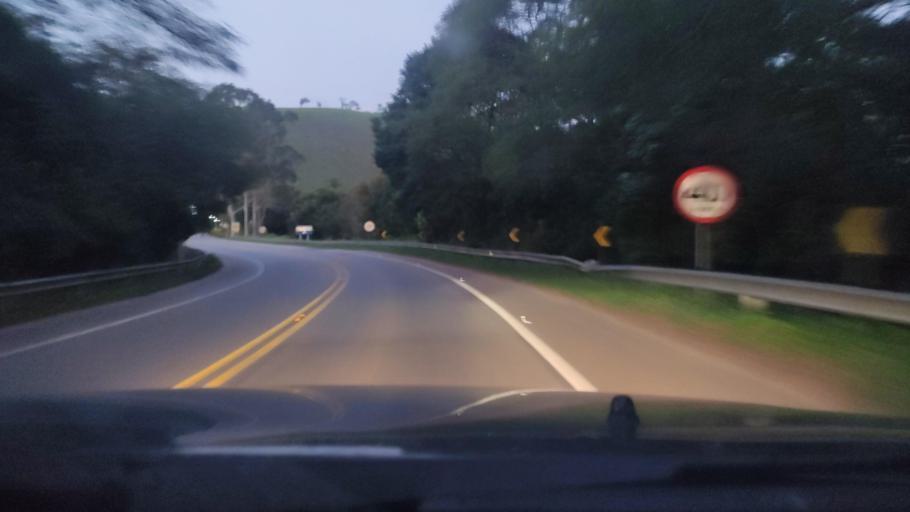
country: BR
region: Sao Paulo
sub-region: Campos Do Jordao
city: Campos do Jordao
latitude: -22.7244
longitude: -45.7270
